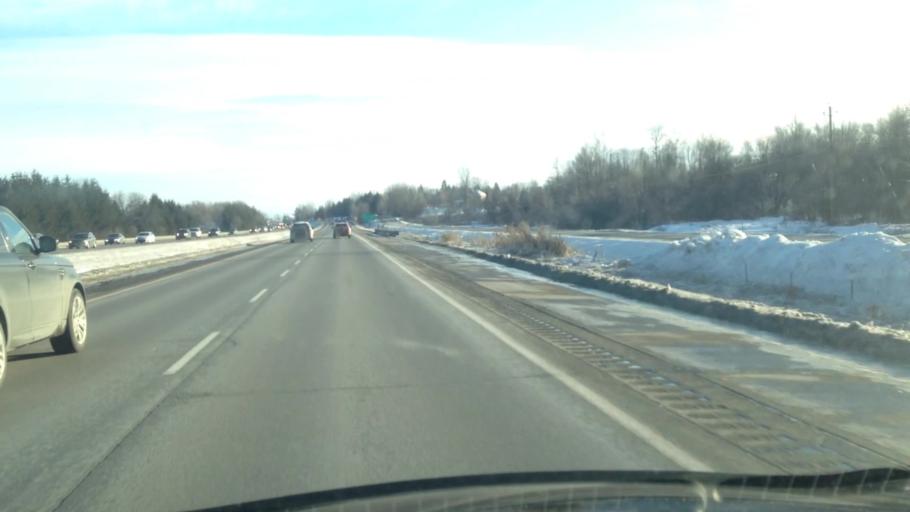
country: CA
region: Quebec
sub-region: Laurentides
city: Prevost
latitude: 45.8190
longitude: -74.0536
